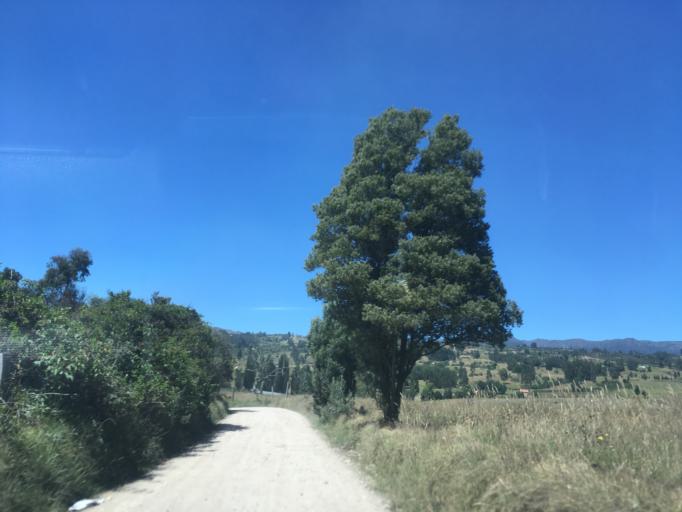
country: CO
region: Boyaca
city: Tuta
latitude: 5.6703
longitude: -73.2761
